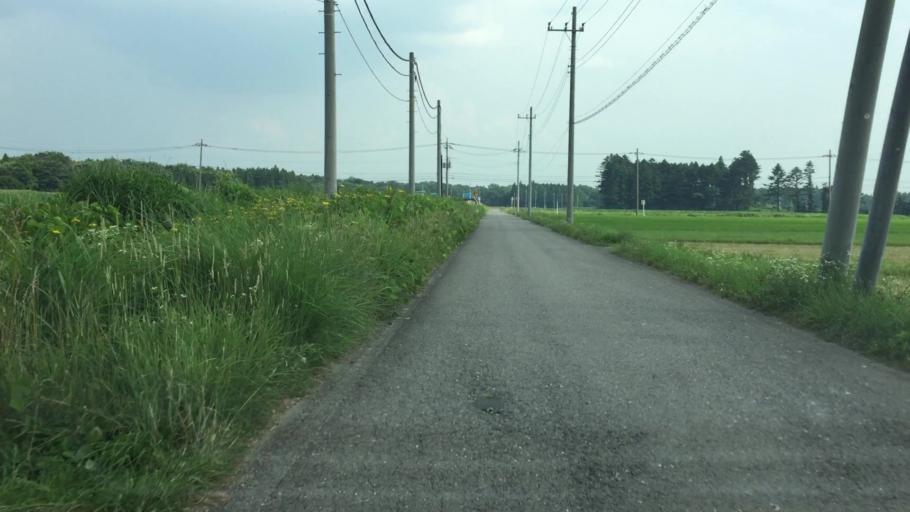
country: JP
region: Tochigi
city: Kuroiso
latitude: 37.0251
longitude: 139.9452
